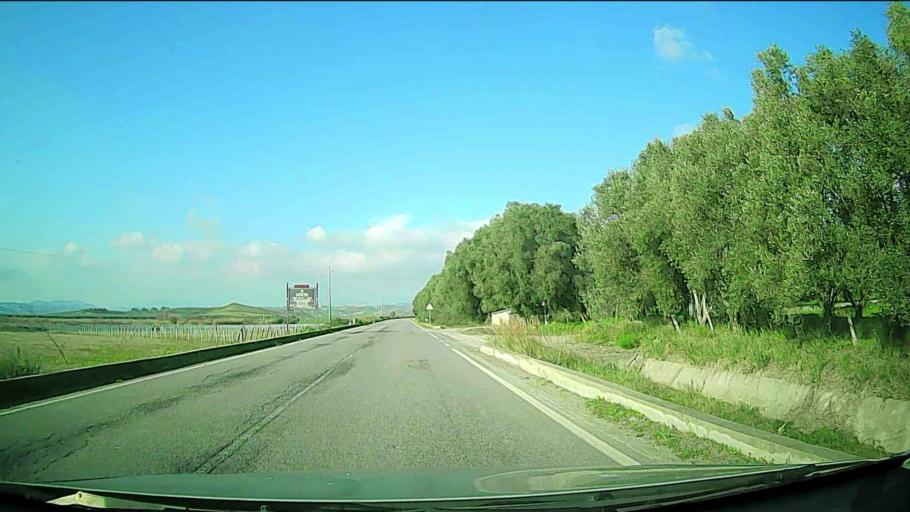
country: IT
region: Calabria
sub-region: Provincia di Crotone
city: Tronca
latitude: 39.1989
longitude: 17.0815
